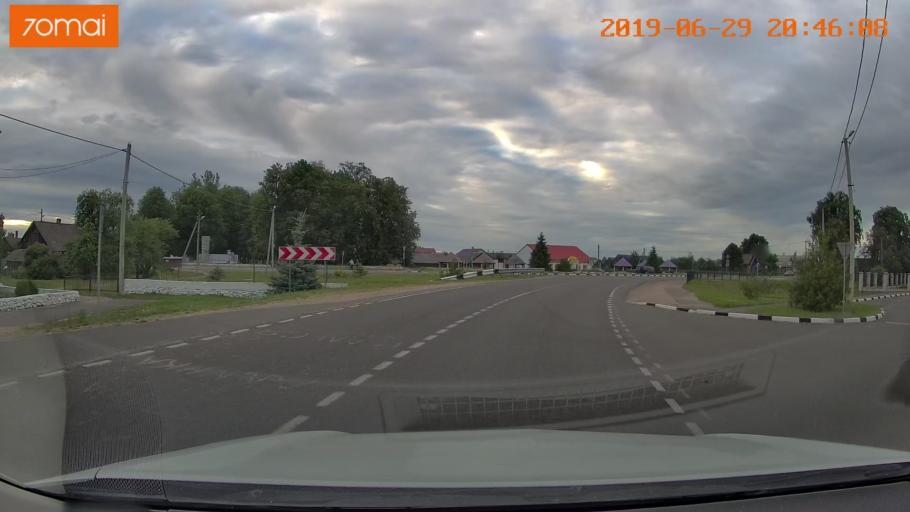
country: BY
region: Brest
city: Hantsavichy
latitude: 52.6291
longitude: 26.3075
